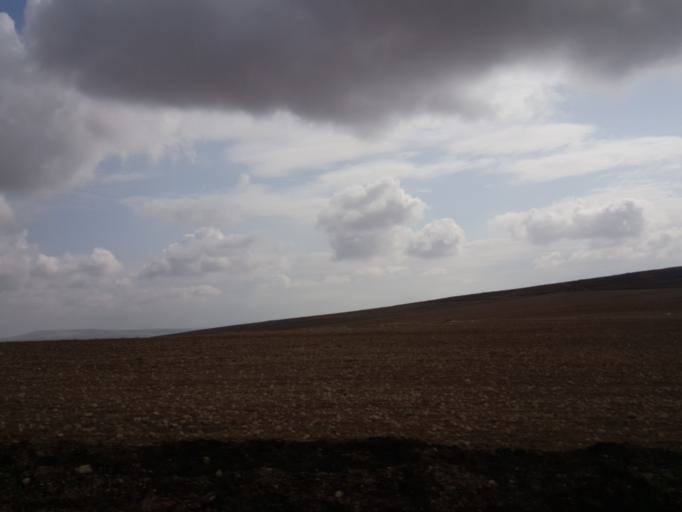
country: TR
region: Kirikkale
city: Keskin
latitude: 39.6439
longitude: 33.6182
